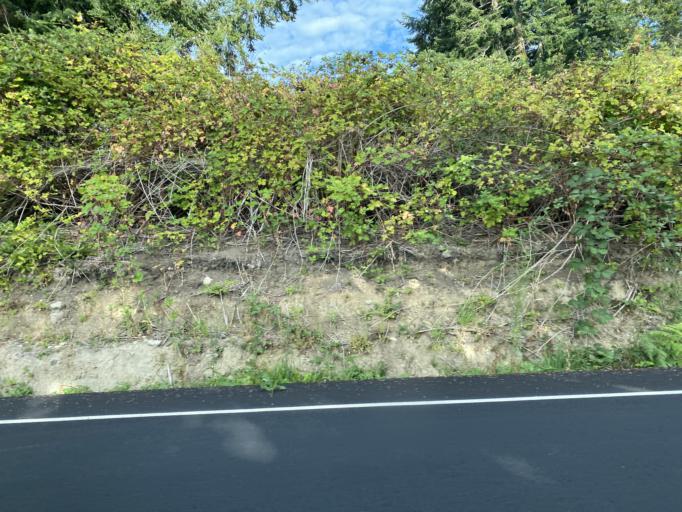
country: US
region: Washington
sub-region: Island County
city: Freeland
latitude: 48.0114
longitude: -122.5368
